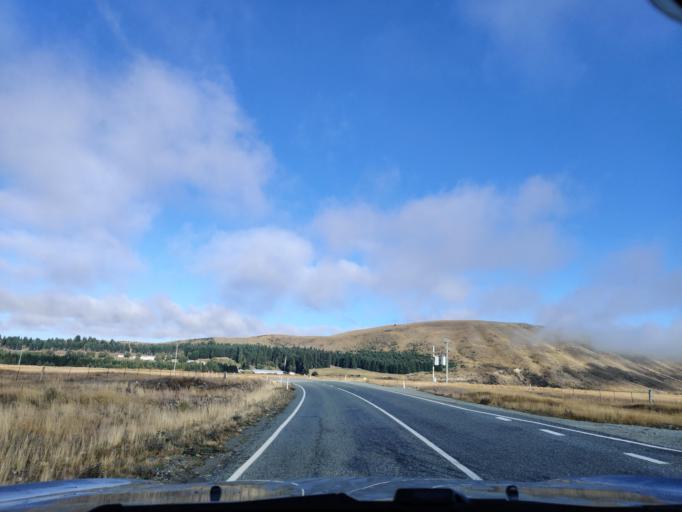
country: NZ
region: Canterbury
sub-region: Timaru District
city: Pleasant Point
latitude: -43.9973
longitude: 170.4191
